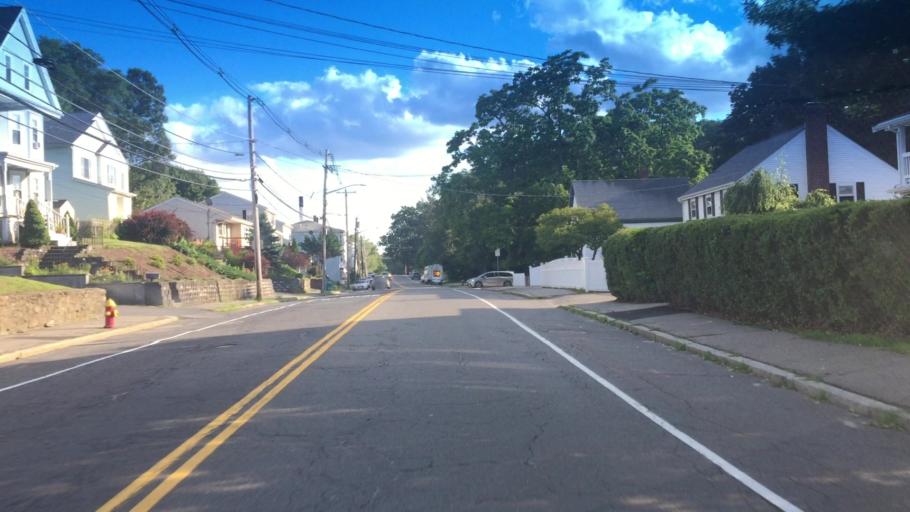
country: US
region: Massachusetts
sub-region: Norfolk County
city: Norwood
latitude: 42.1708
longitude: -71.2100
